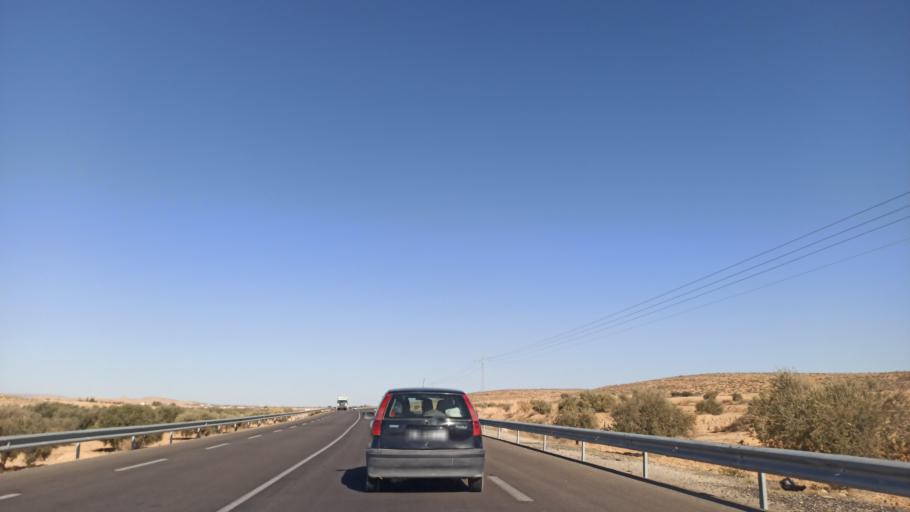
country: TN
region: Sidi Bu Zayd
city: Bi'r al Hufayy
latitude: 34.7193
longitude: 9.0597
